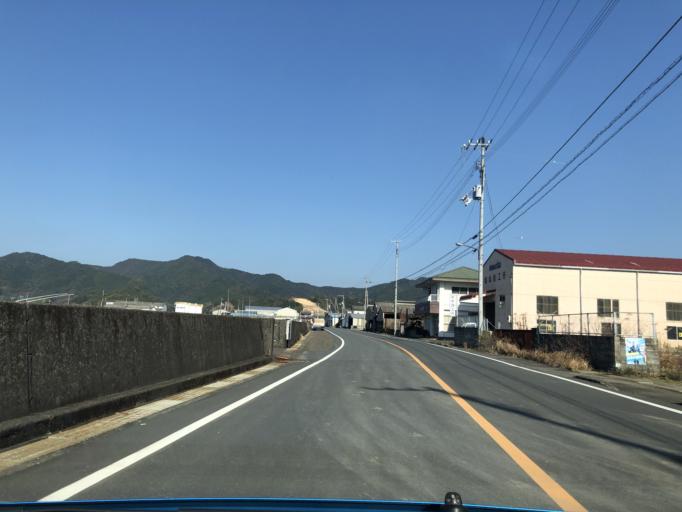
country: JP
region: Kochi
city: Sukumo
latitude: 32.9228
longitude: 132.6950
